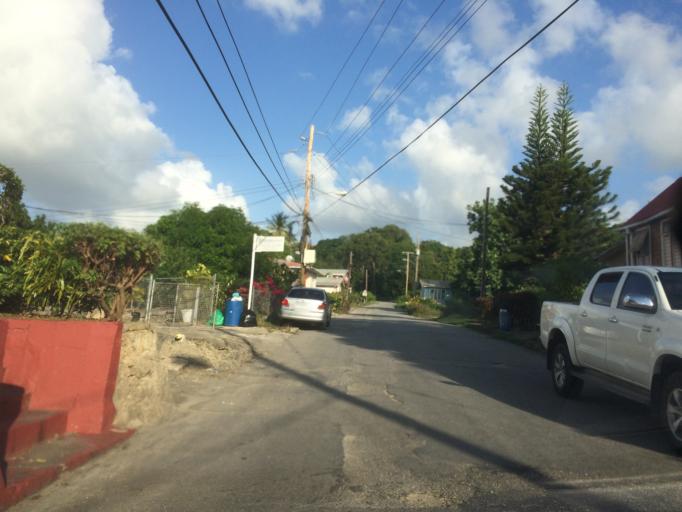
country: BB
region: Saint Peter
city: Speightstown
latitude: 13.2497
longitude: -59.6391
